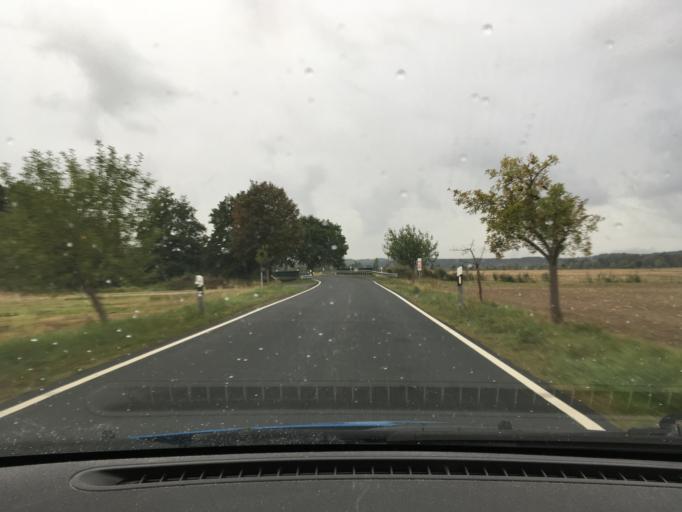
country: DE
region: Lower Saxony
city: Hitzacker
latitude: 53.1916
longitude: 11.0370
